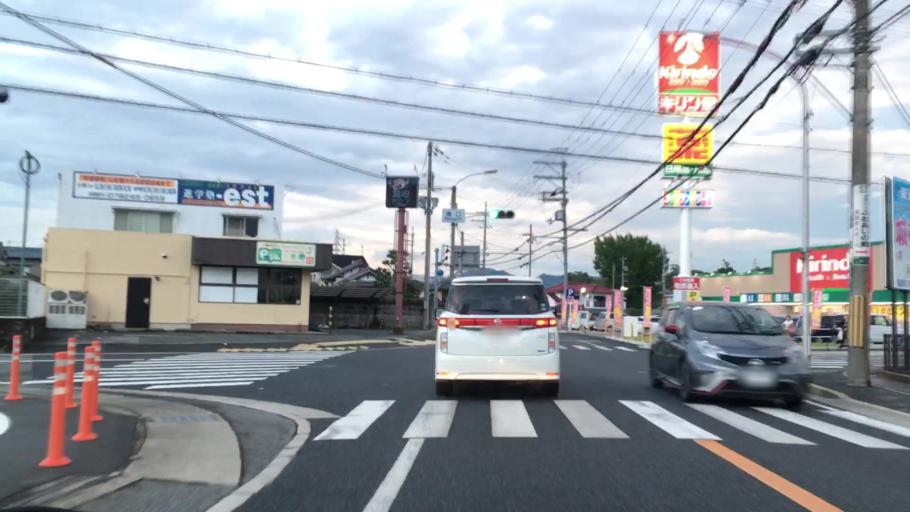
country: JP
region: Hyogo
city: Himeji
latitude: 34.9268
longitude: 134.7466
